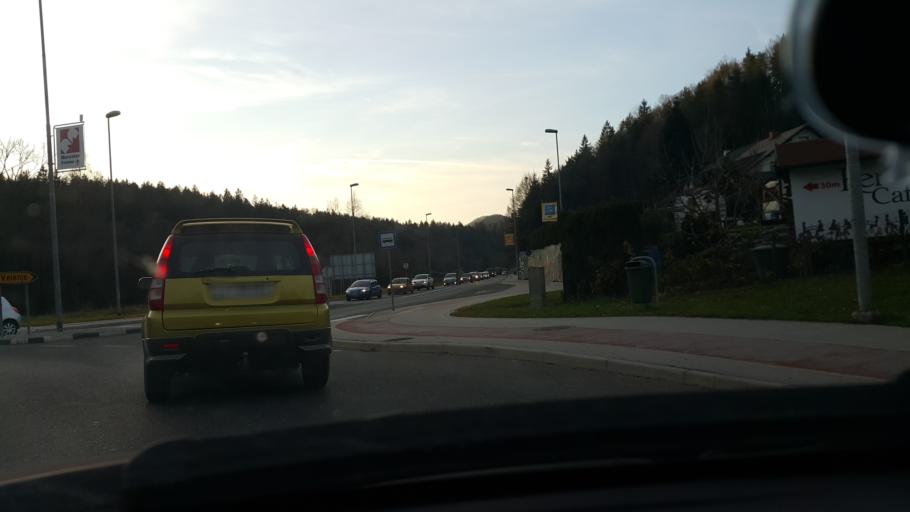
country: SI
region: Velenje
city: Velenje
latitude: 46.3532
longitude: 15.1264
